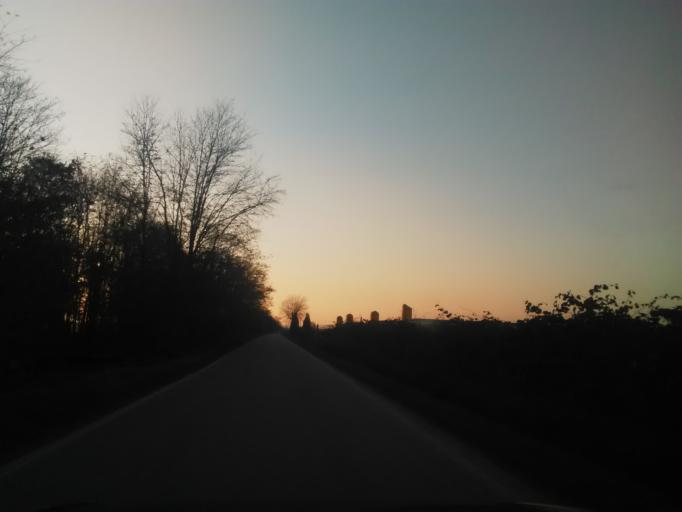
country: IT
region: Piedmont
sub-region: Provincia di Vercelli
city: Santhia
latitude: 45.3604
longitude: 8.1337
